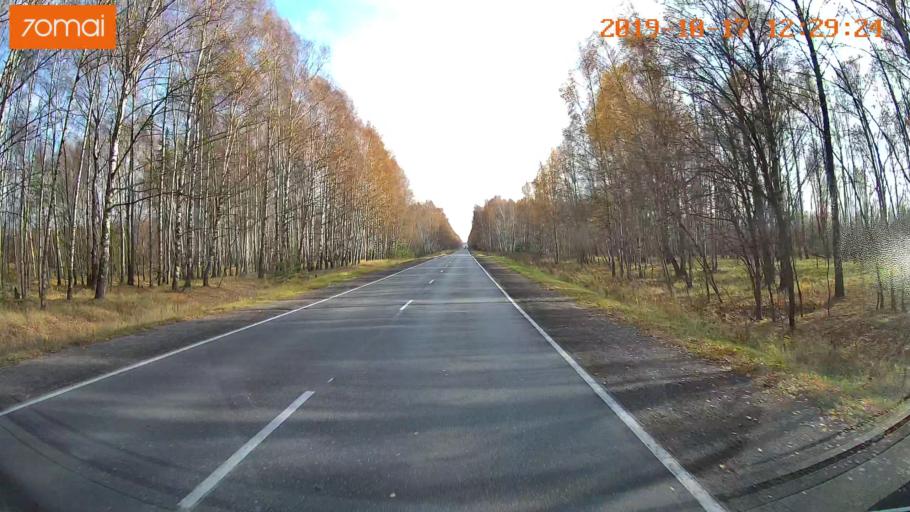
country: RU
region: Rjazan
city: Syntul
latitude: 54.9819
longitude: 41.2913
